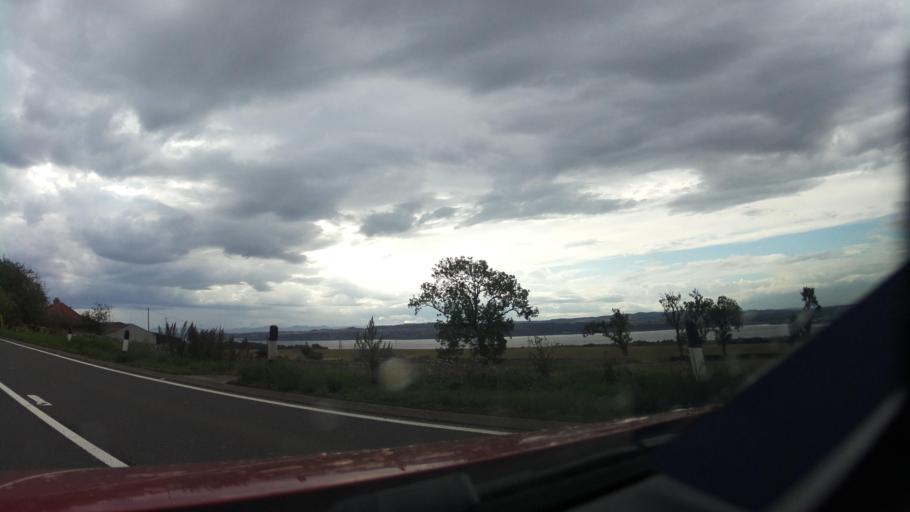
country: GB
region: Scotland
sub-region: Fife
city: Kincardine
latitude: 56.0638
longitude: -3.6809
